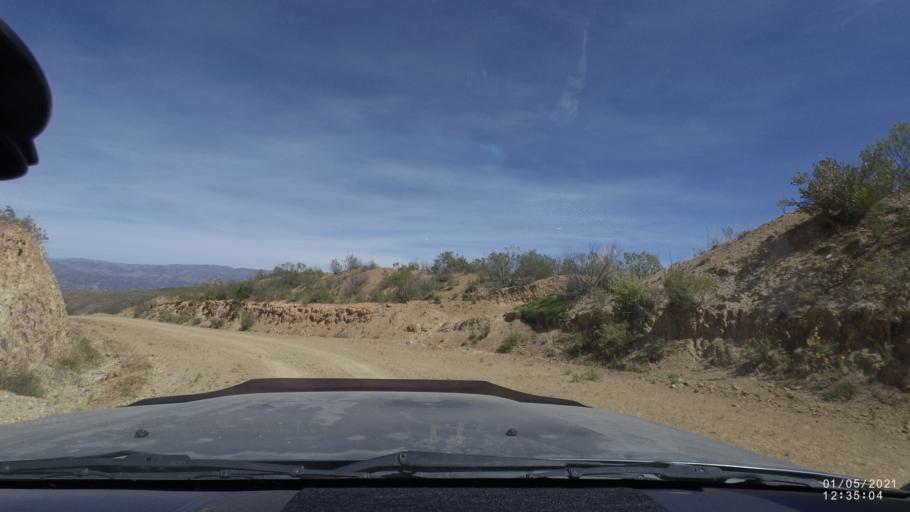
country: BO
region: Cochabamba
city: Capinota
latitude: -17.6769
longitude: -66.1552
